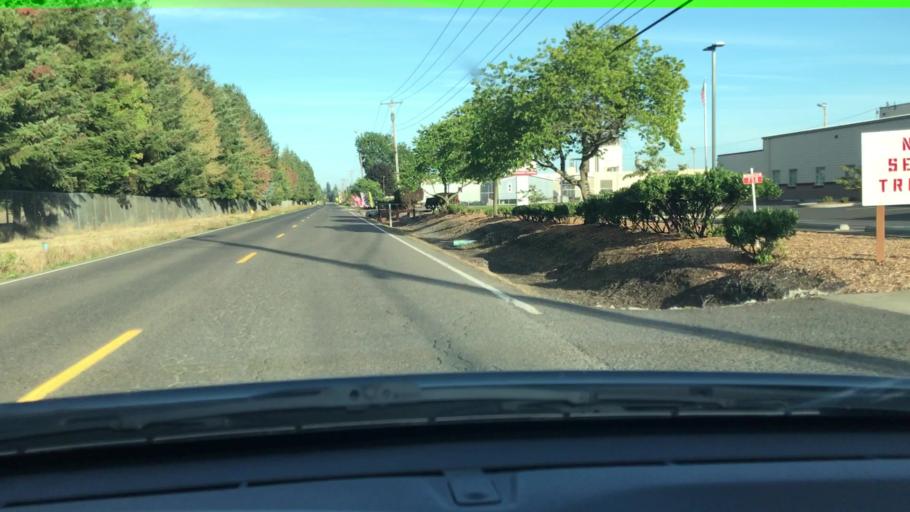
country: US
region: Oregon
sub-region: Yamhill County
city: McMinnville
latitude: 45.1929
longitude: -123.2065
